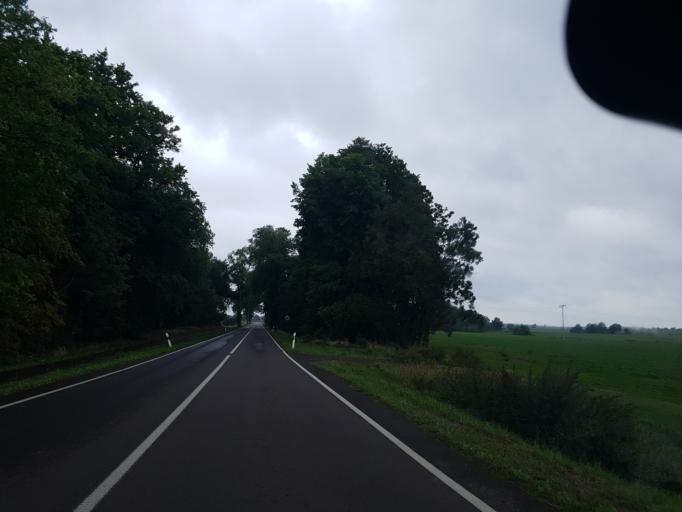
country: DE
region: Saxony-Anhalt
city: Tucheim
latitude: 52.3151
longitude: 12.1065
